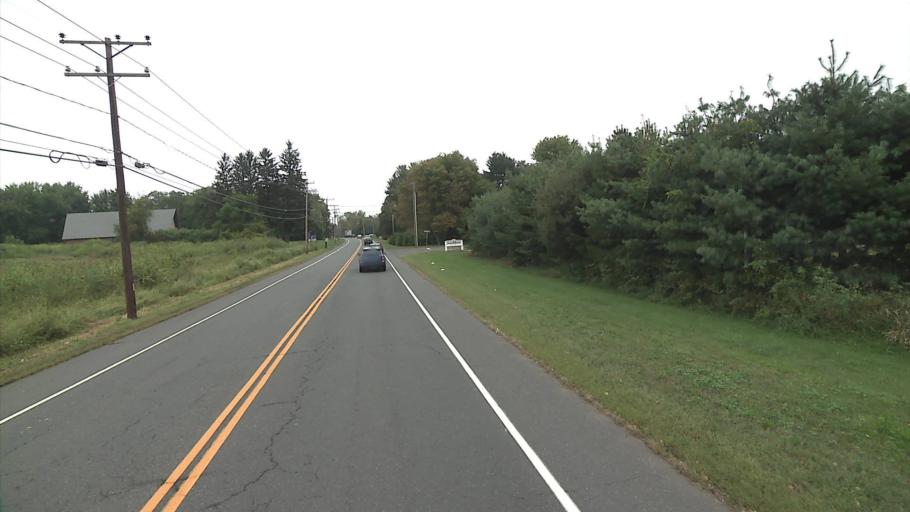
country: US
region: Connecticut
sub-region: Hartford County
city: Suffield Depot
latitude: 41.9665
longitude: -72.6612
